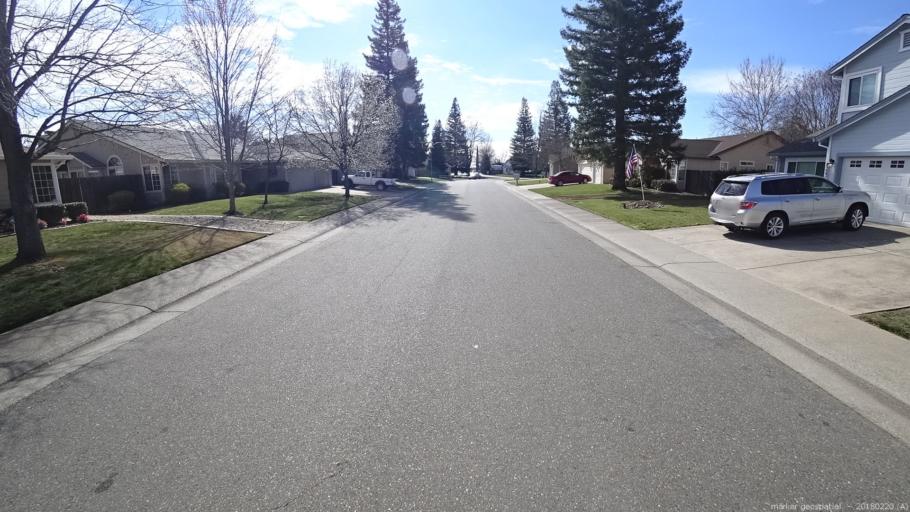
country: US
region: California
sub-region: Sacramento County
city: Orangevale
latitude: 38.6817
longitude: -121.2191
